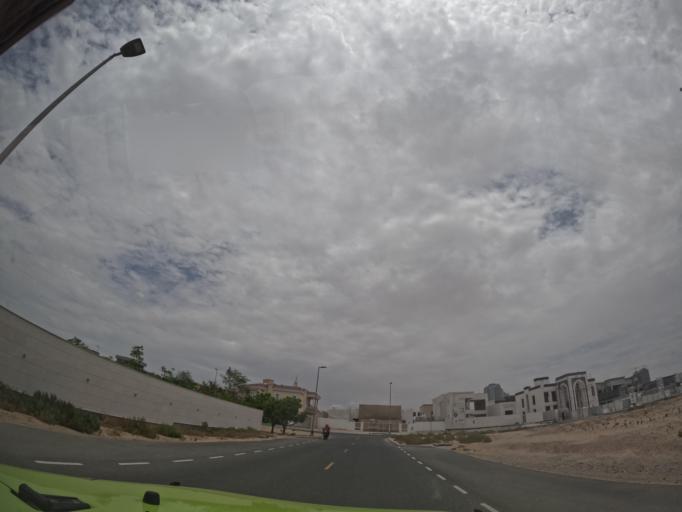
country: AE
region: Dubai
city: Dubai
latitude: 25.1298
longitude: 55.3698
